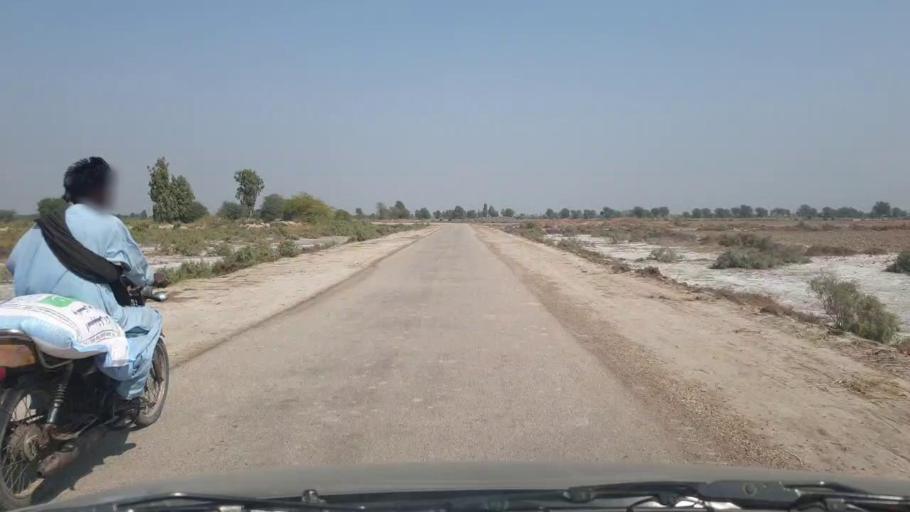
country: PK
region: Sindh
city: Mirwah Gorchani
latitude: 25.3373
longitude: 69.1479
